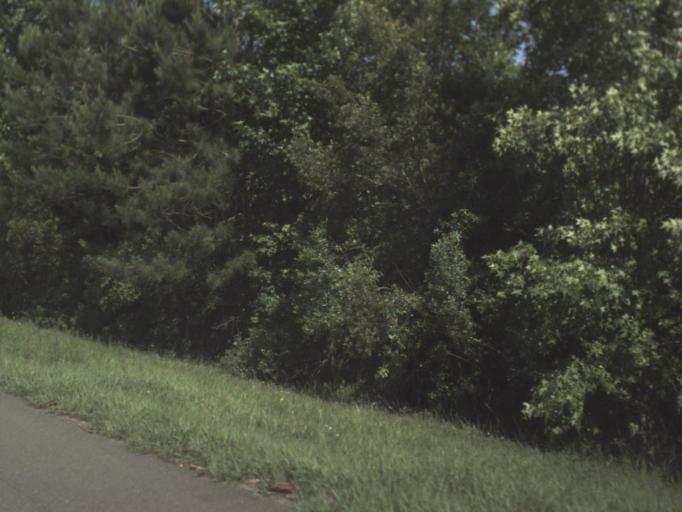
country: US
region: Florida
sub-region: Duval County
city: Baldwin
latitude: 30.3013
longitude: -82.0280
